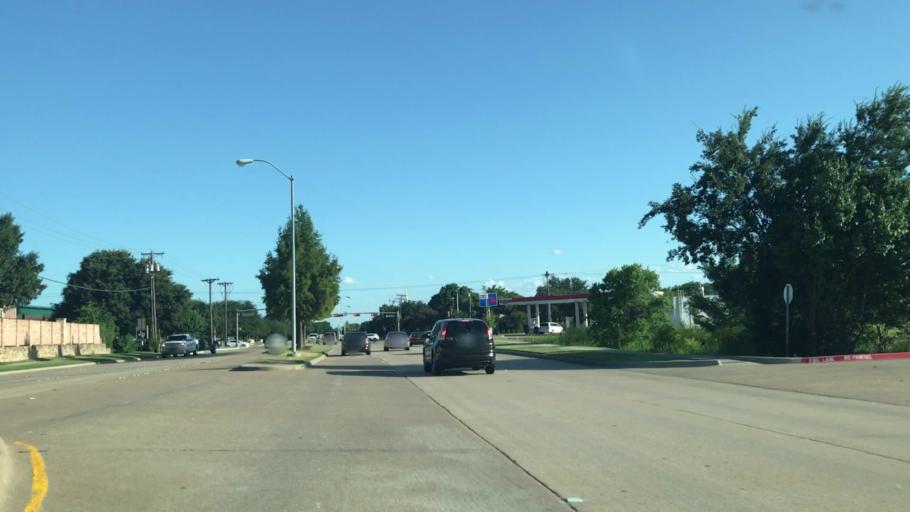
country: US
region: Texas
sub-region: Collin County
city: Plano
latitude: 33.0730
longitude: -96.7369
